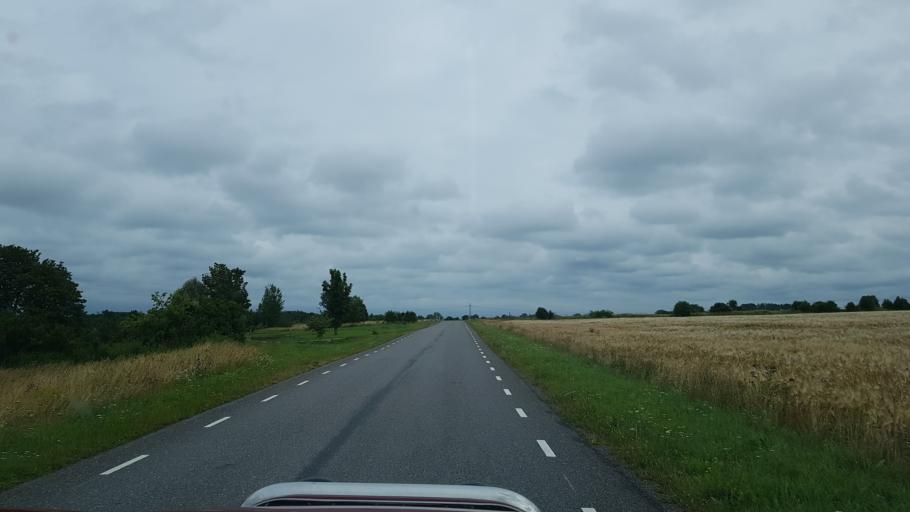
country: EE
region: Ida-Virumaa
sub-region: Puessi linn
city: Pussi
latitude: 59.4021
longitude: 27.0097
